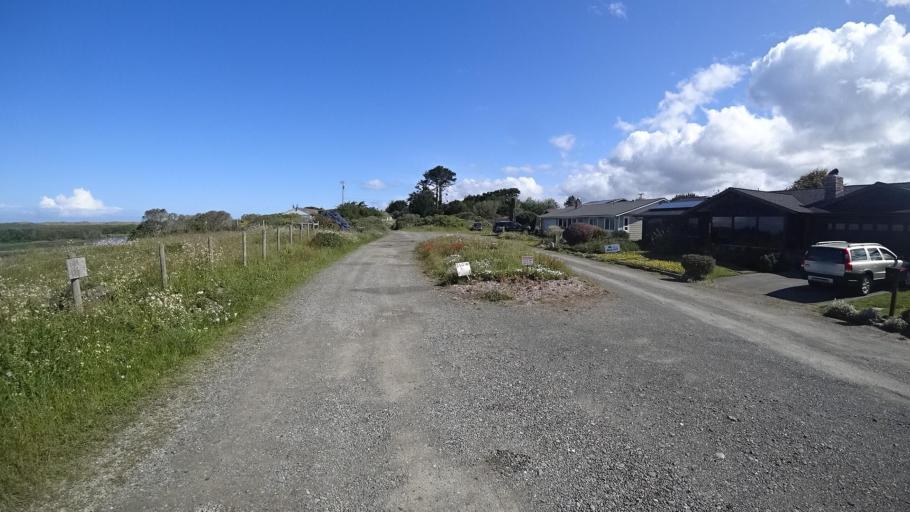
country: US
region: California
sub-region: Humboldt County
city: McKinleyville
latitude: 40.9342
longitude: -124.1276
